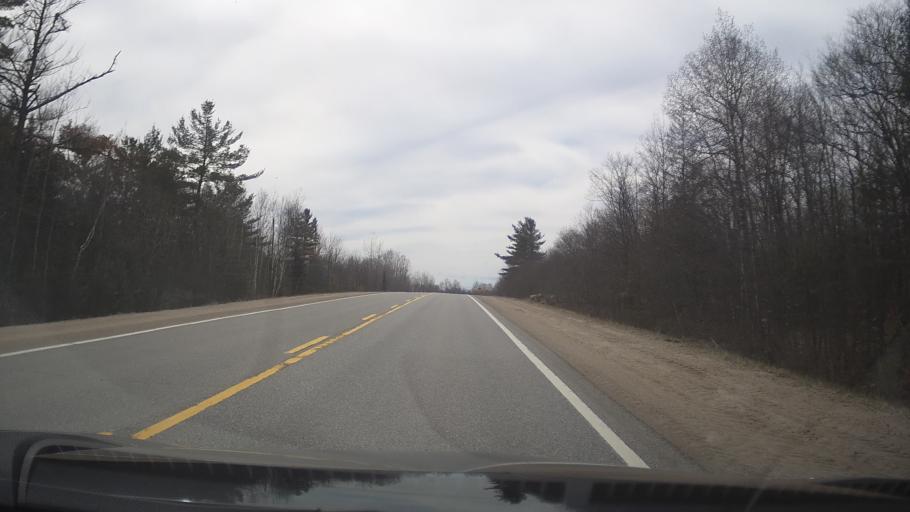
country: CA
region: Ontario
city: Arnprior
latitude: 45.5247
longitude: -76.2882
